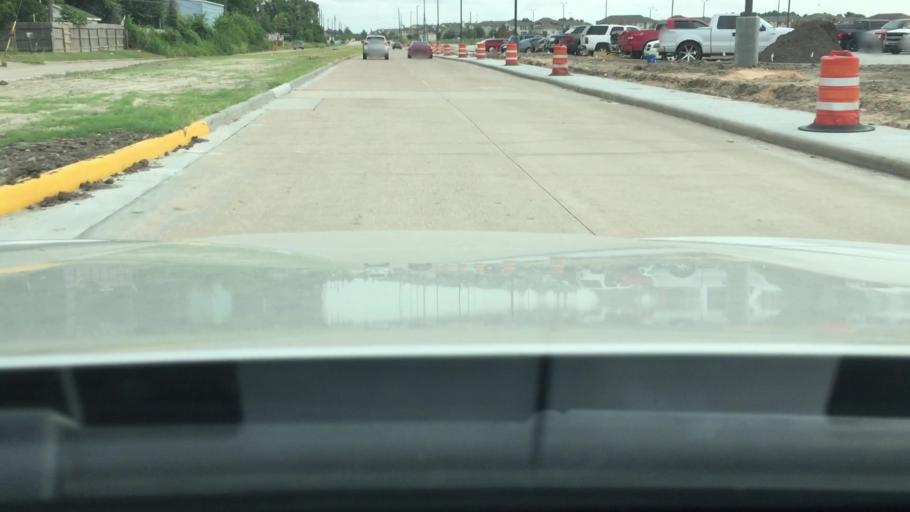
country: US
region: Texas
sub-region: Harris County
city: Jersey Village
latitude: 29.9433
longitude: -95.5467
